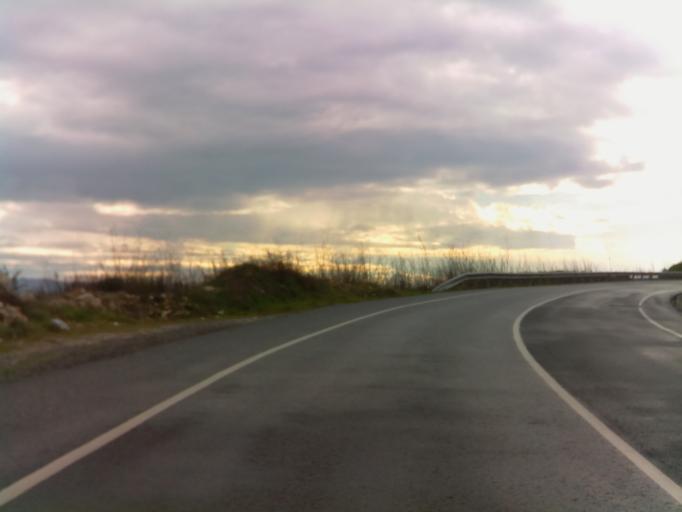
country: CY
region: Pafos
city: Pegeia
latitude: 34.9056
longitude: 32.4420
